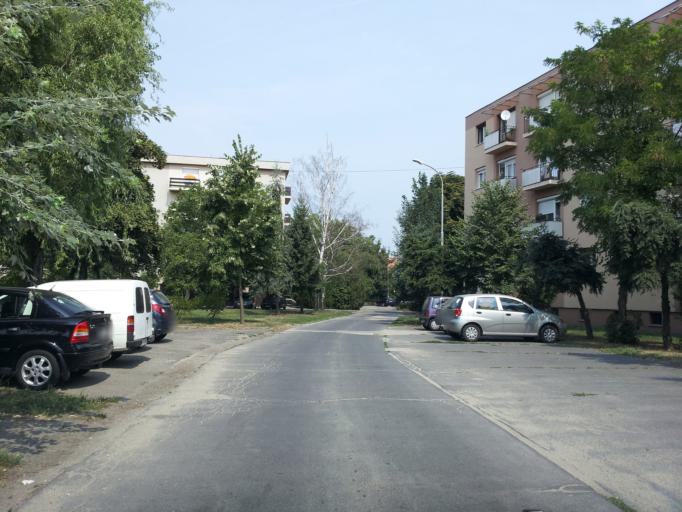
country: HU
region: Gyor-Moson-Sopron
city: Csorna
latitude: 47.6132
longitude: 17.2534
